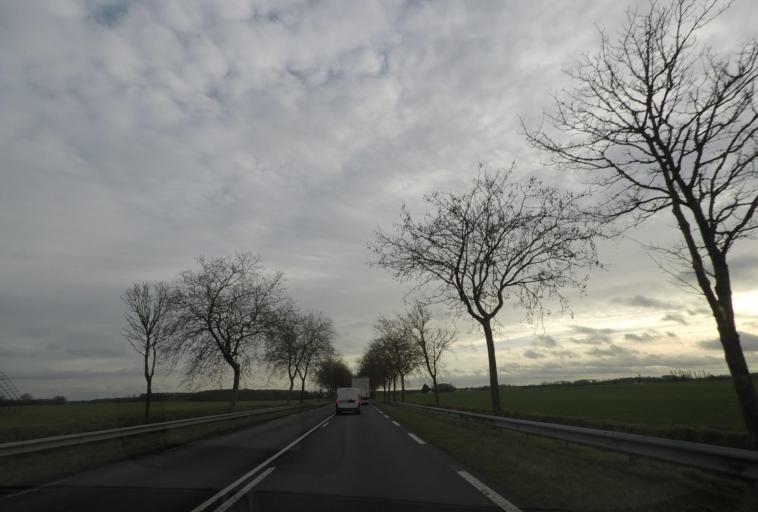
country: FR
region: Centre
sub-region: Departement du Loir-et-Cher
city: Sarge-sur-Braye
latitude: 47.9043
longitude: 0.8945
